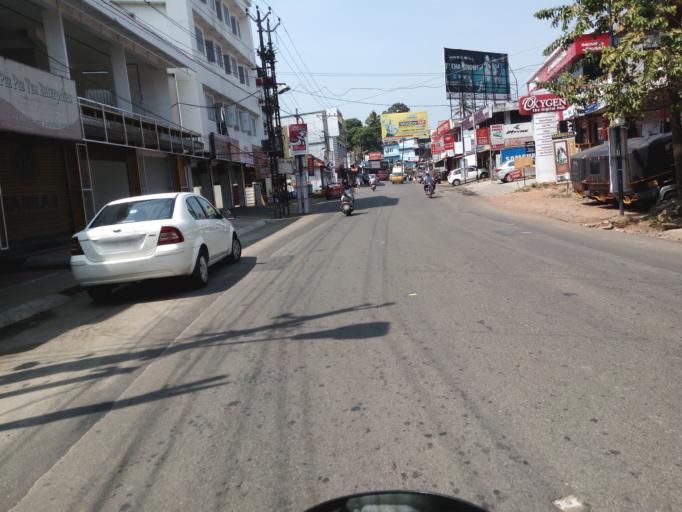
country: IN
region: Kerala
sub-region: Ernakulam
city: Muvattupula
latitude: 9.9021
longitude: 76.7118
